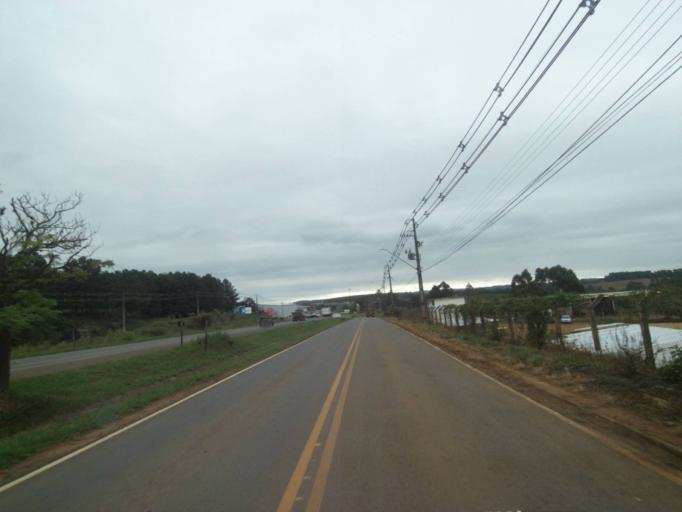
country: BR
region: Parana
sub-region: Telemaco Borba
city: Telemaco Borba
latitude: -24.3787
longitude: -50.6687
